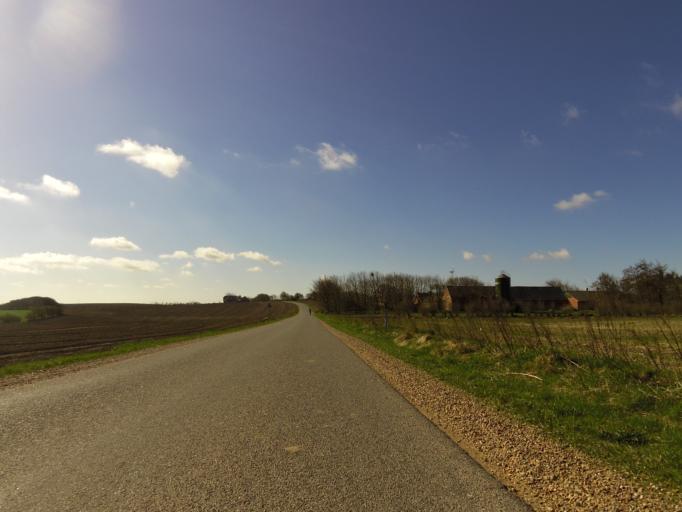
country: DK
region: Central Jutland
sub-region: Holstebro Kommune
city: Vinderup
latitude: 56.4613
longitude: 8.7220
